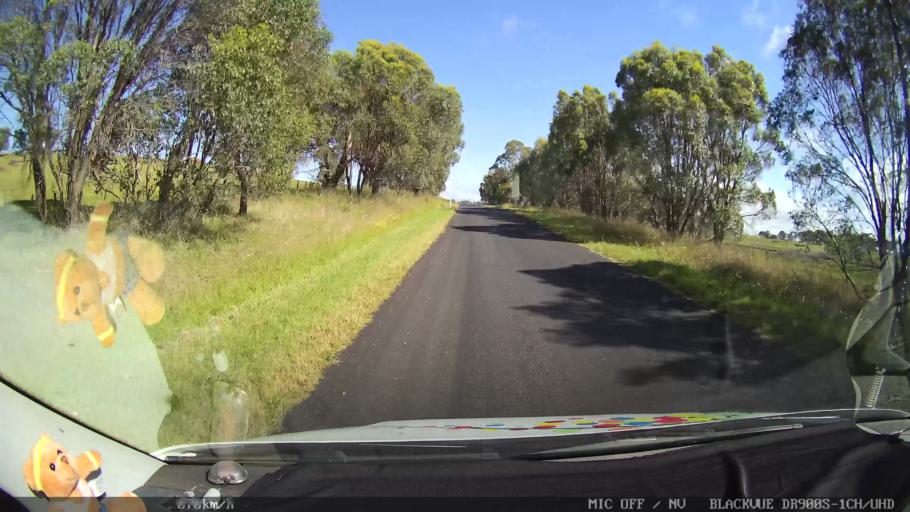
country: AU
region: New South Wales
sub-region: Guyra
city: Guyra
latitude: -30.0797
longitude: 151.6769
